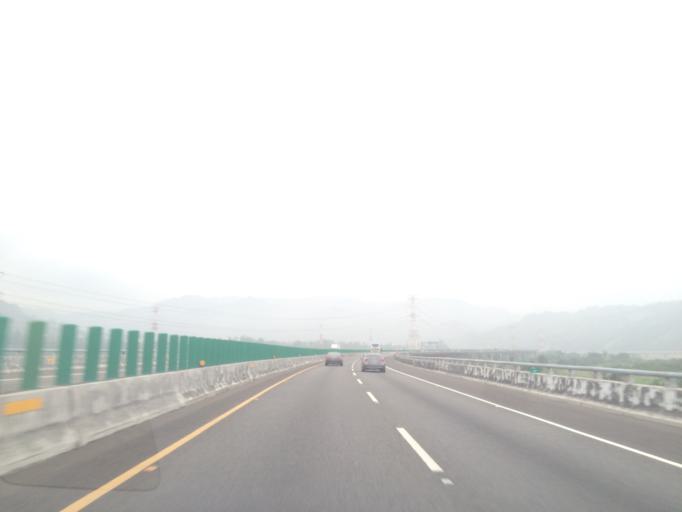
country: TW
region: Taiwan
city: Zhongxing New Village
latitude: 23.9948
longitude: 120.7488
